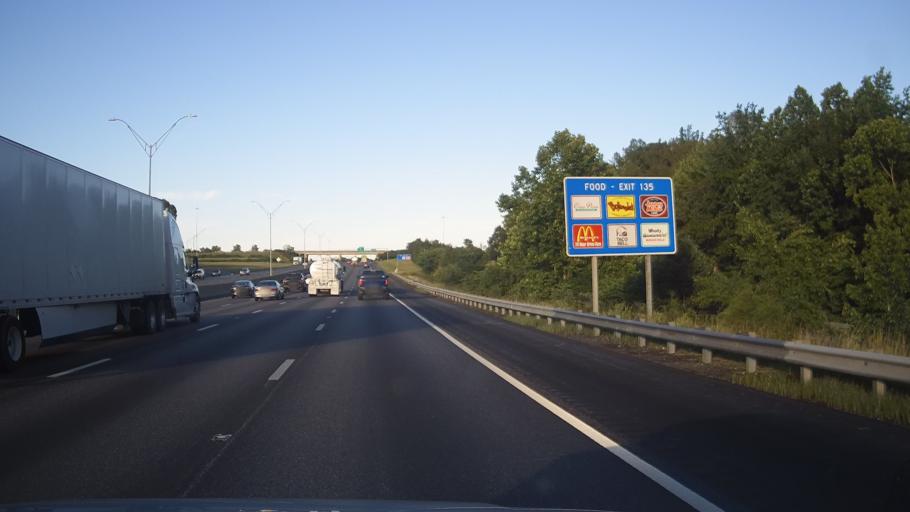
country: US
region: North Carolina
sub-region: Guilford County
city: McLeansville
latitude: 36.0594
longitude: -79.6148
